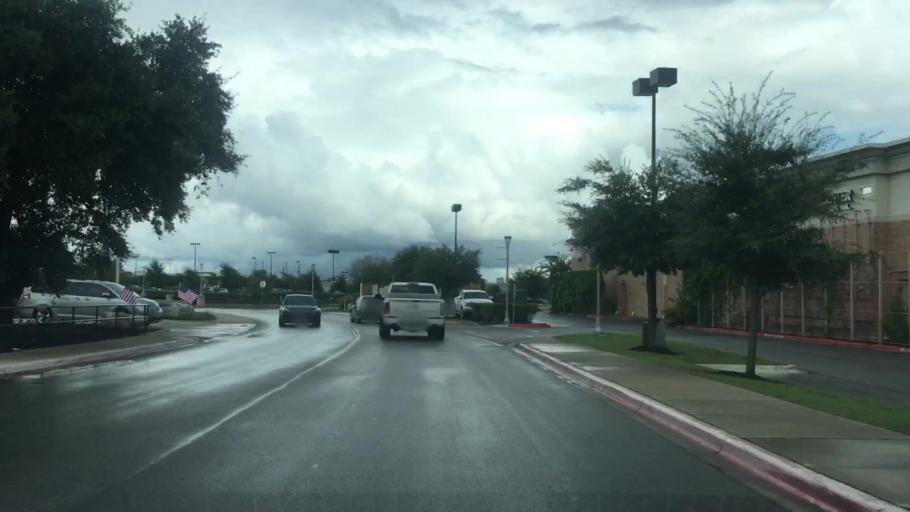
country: US
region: Texas
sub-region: Williamson County
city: Cedar Park
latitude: 30.5255
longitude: -97.8208
